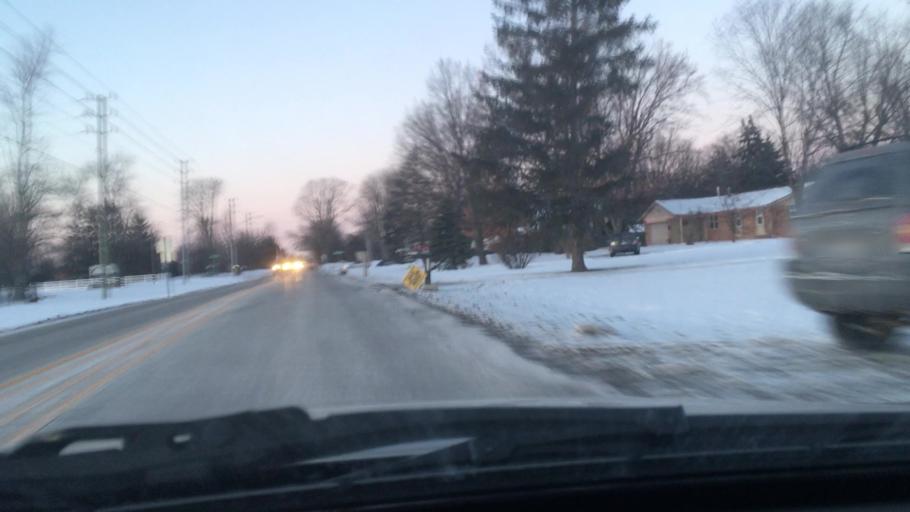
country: US
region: Indiana
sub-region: Marion County
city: Lawrence
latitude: 39.8853
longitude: -86.0330
